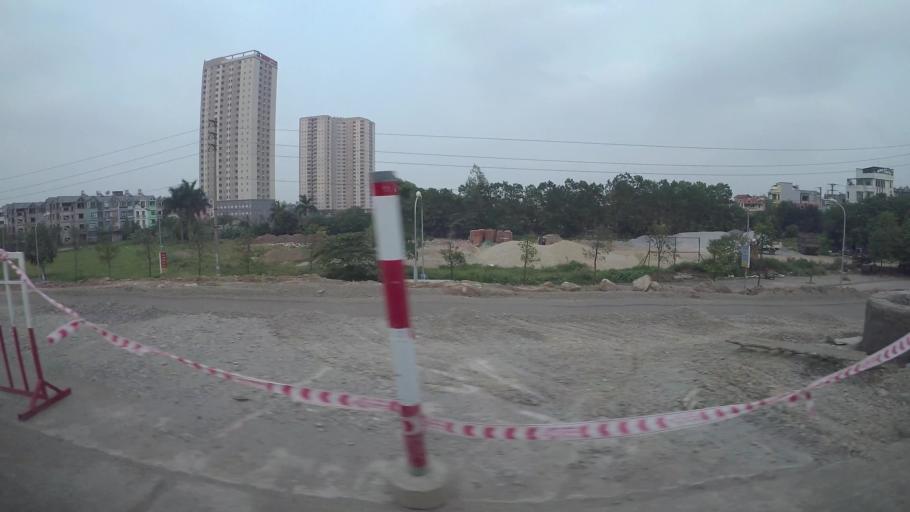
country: VN
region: Ha Noi
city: Trau Quy
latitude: 21.0175
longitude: 105.9043
